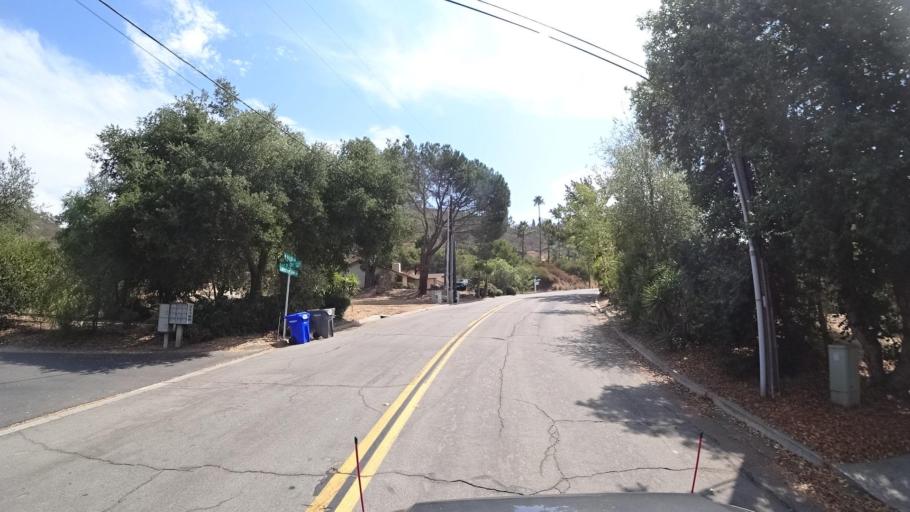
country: US
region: California
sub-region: San Diego County
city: Hidden Meadows
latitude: 33.1873
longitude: -117.0887
